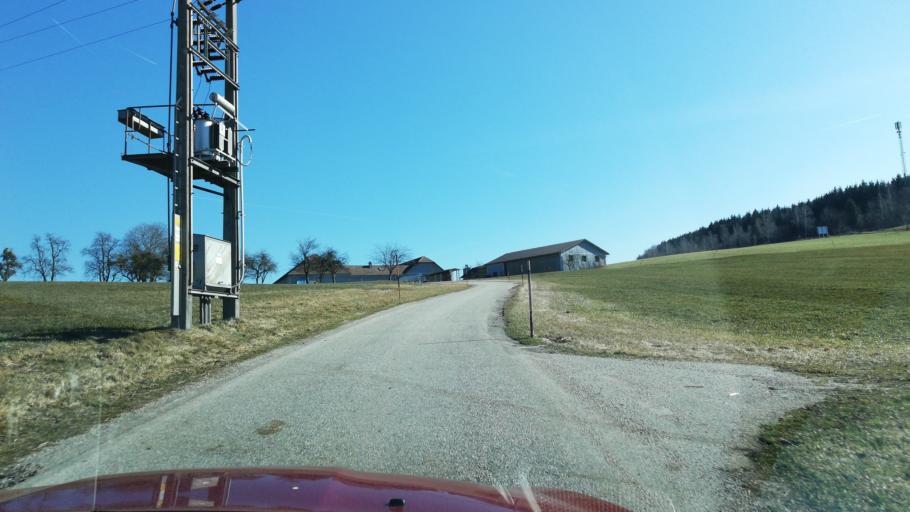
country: AT
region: Upper Austria
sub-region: Politischer Bezirk Vocklabruck
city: Aurach am Hongar
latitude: 47.9524
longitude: 13.6939
